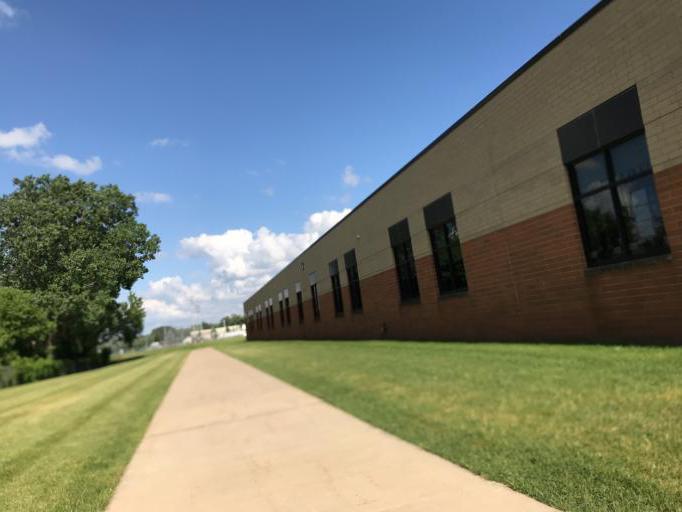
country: US
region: Michigan
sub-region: Oakland County
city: South Lyon
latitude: 42.4474
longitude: -83.6590
